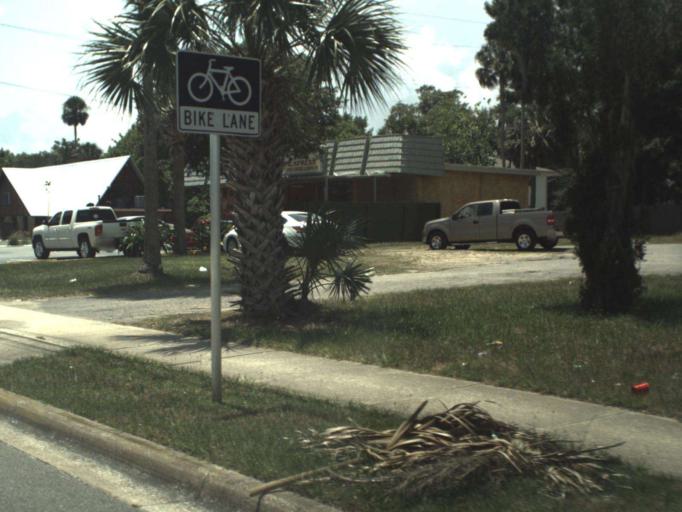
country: US
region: Florida
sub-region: Volusia County
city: South Daytona
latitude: 29.1865
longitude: -81.0099
